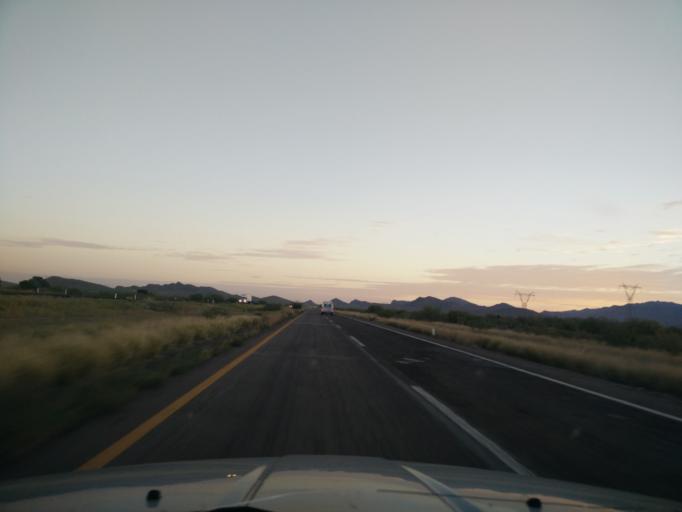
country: MX
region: Sonora
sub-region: Empalme
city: La Palma
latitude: 28.3856
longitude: -111.0432
